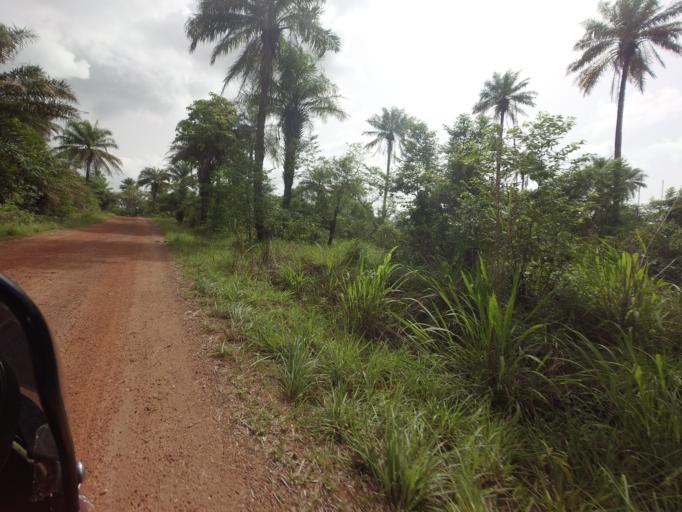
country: SL
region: Northern Province
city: Kambia
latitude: 9.0792
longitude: -13.0210
